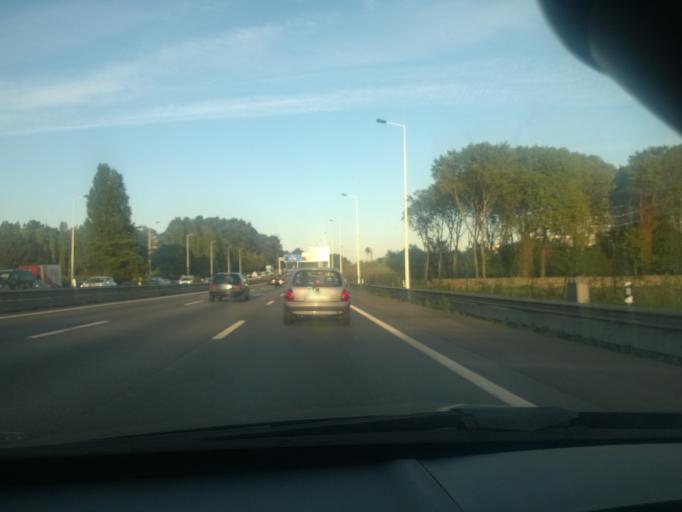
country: PT
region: Porto
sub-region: Matosinhos
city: Senhora da Hora
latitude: 41.1719
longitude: -8.6319
